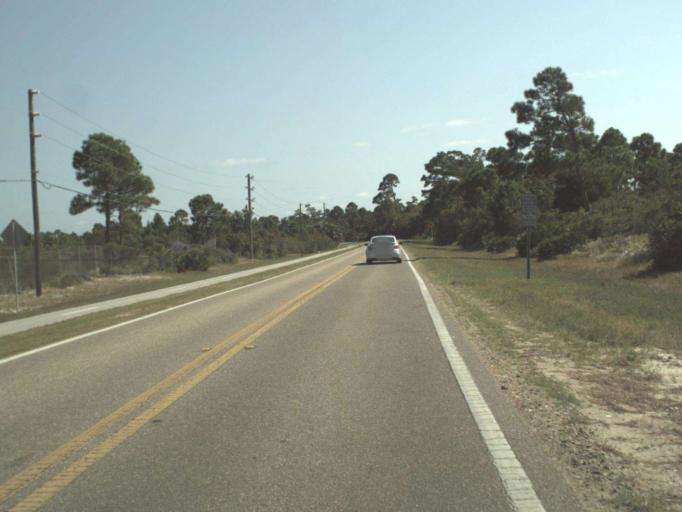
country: US
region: Florida
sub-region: Gulf County
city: Port Saint Joe
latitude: 29.6756
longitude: -85.3544
